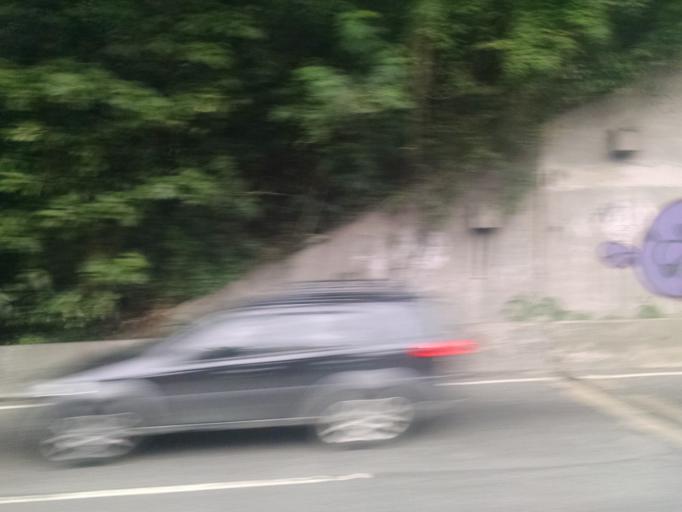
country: BR
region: Rio de Janeiro
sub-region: Rio De Janeiro
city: Rio de Janeiro
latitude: -22.9825
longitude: -43.2352
